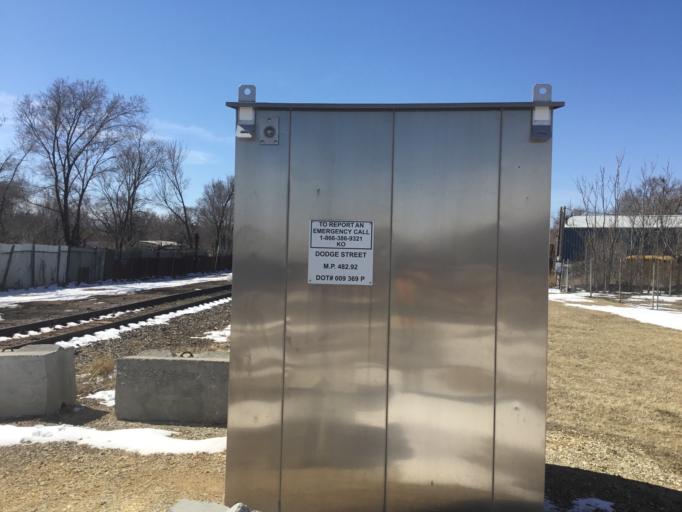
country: US
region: Kansas
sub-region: Sedgwick County
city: Wichita
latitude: 37.6692
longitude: -97.3551
